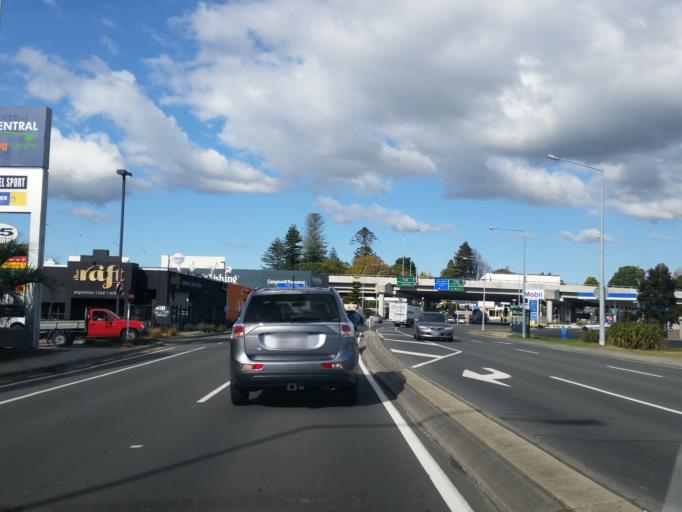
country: NZ
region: Bay of Plenty
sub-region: Tauranga City
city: Tauranga
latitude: -37.6742
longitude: 176.1649
